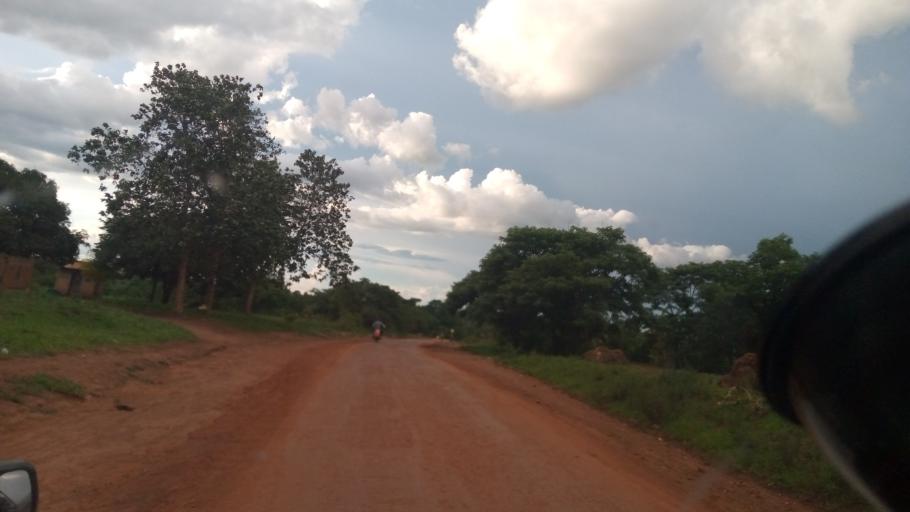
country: UG
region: Northern Region
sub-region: Kole District
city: Kole
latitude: 2.3803
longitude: 32.9327
